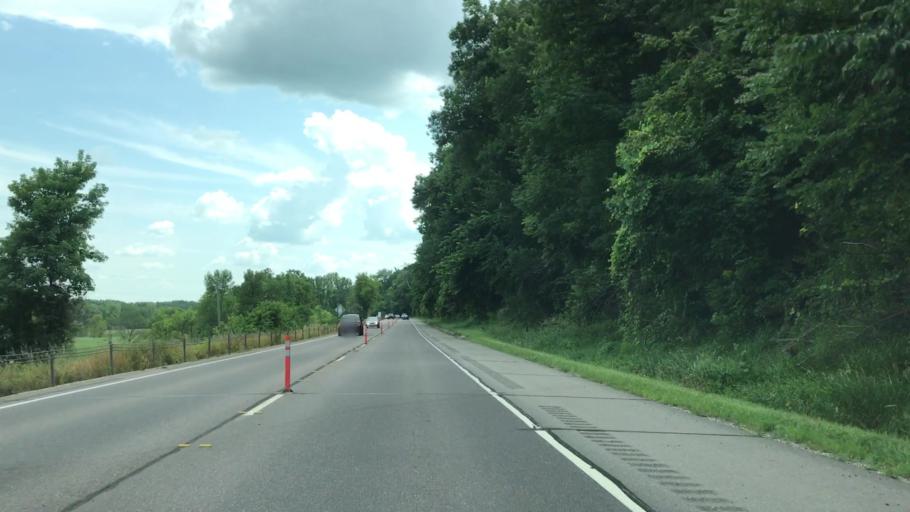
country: US
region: Minnesota
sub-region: Nicollet County
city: Saint Peter
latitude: 44.3800
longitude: -93.9692
